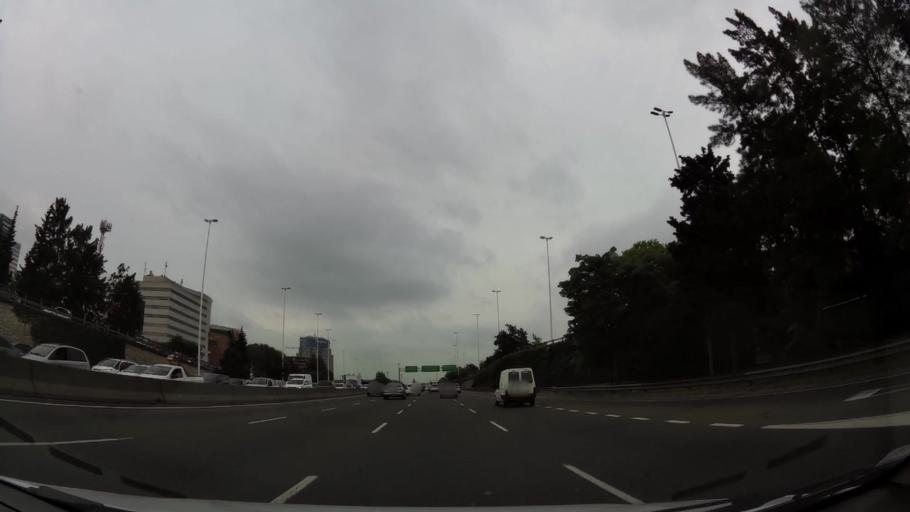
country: AR
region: Buenos Aires
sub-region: Partido de Vicente Lopez
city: Olivos
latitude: -34.5437
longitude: -58.4868
